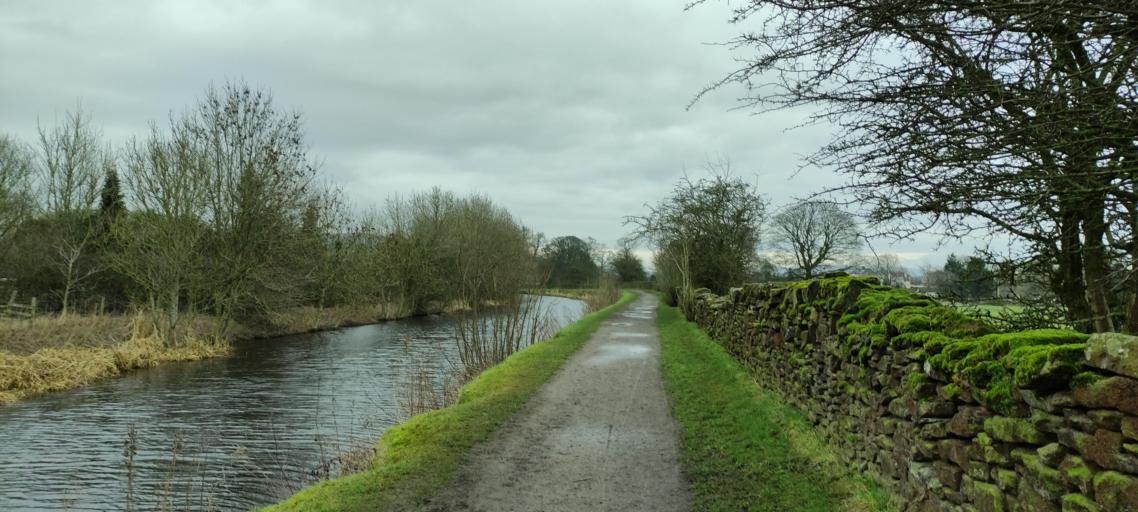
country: GB
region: England
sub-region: North Yorkshire
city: Gargrave
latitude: 53.9833
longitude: -2.1195
